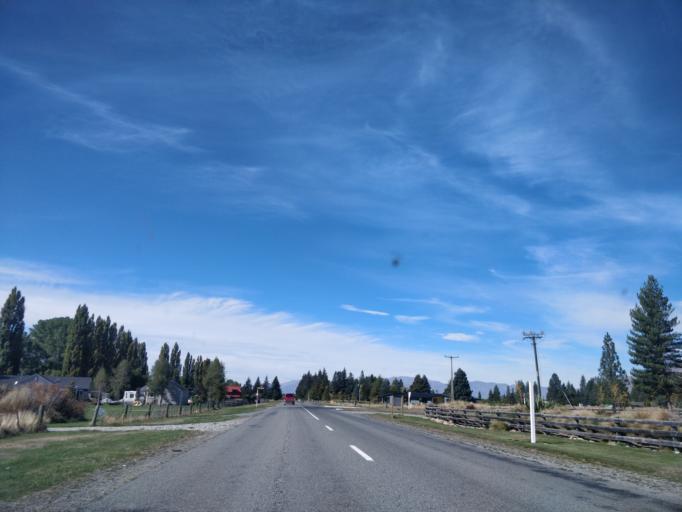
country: NZ
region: Otago
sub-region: Queenstown-Lakes District
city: Wanaka
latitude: -44.2424
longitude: 170.0871
